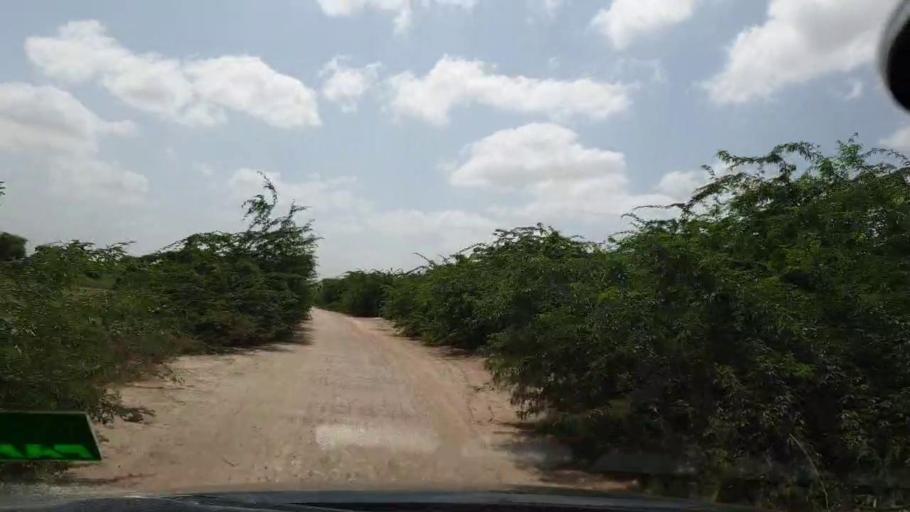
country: PK
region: Sindh
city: Kadhan
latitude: 24.5645
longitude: 69.2110
